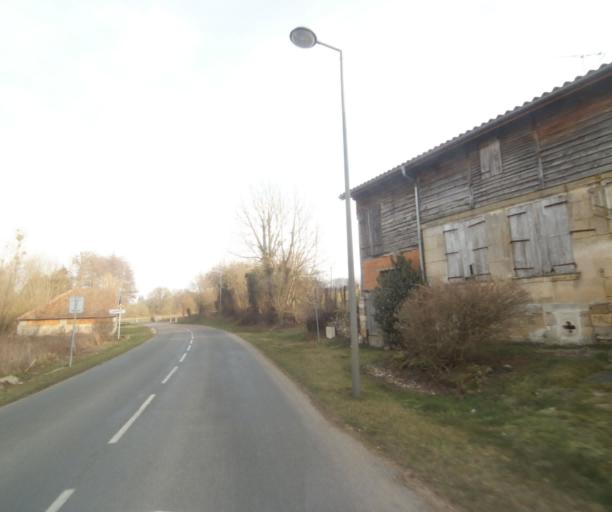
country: FR
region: Champagne-Ardenne
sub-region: Departement de la Marne
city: Sermaize-les-Bains
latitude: 48.7403
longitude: 4.9071
